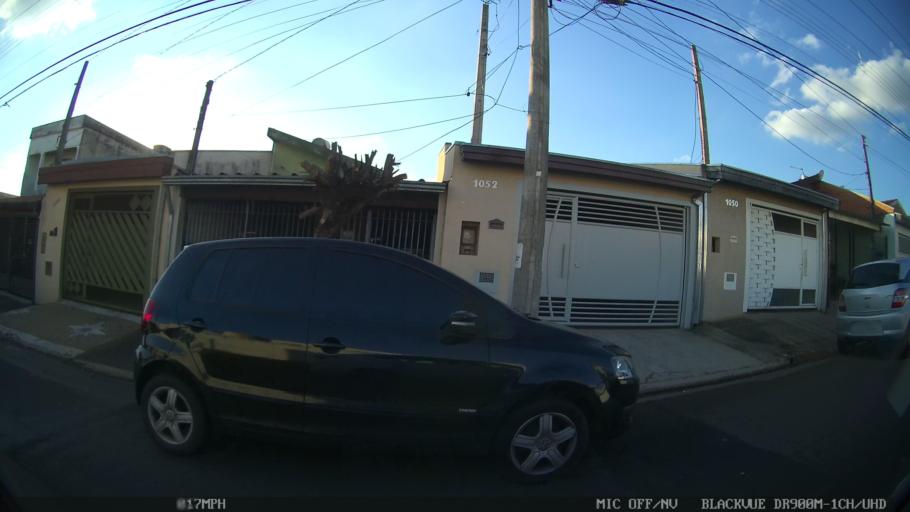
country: BR
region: Sao Paulo
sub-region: Santa Barbara D'Oeste
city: Santa Barbara d'Oeste
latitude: -22.7486
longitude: -47.3767
